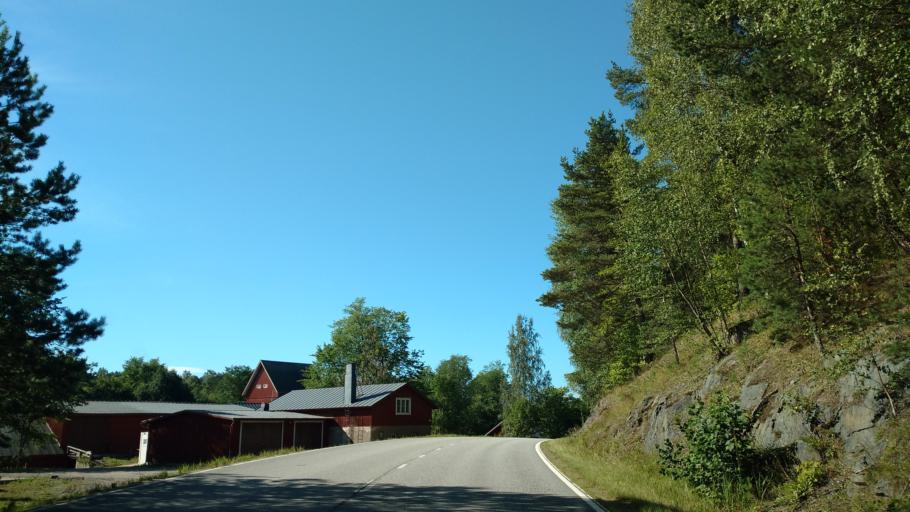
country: FI
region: Uusimaa
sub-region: Raaseporin
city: Pohja
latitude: 60.1334
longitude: 23.5484
